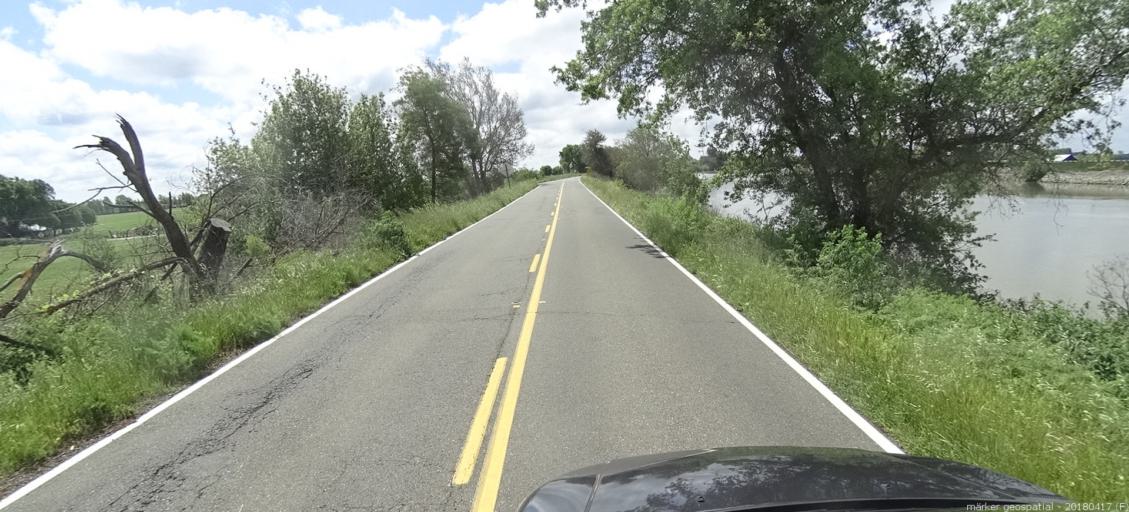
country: US
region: California
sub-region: Sacramento County
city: Walnut Grove
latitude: 38.2047
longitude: -121.5568
